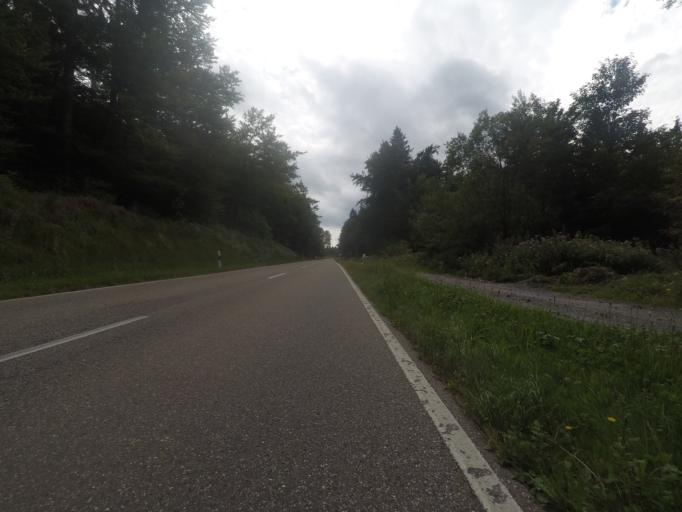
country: DE
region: Baden-Wuerttemberg
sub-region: Karlsruhe Region
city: Dobel
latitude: 48.8071
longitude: 8.4881
